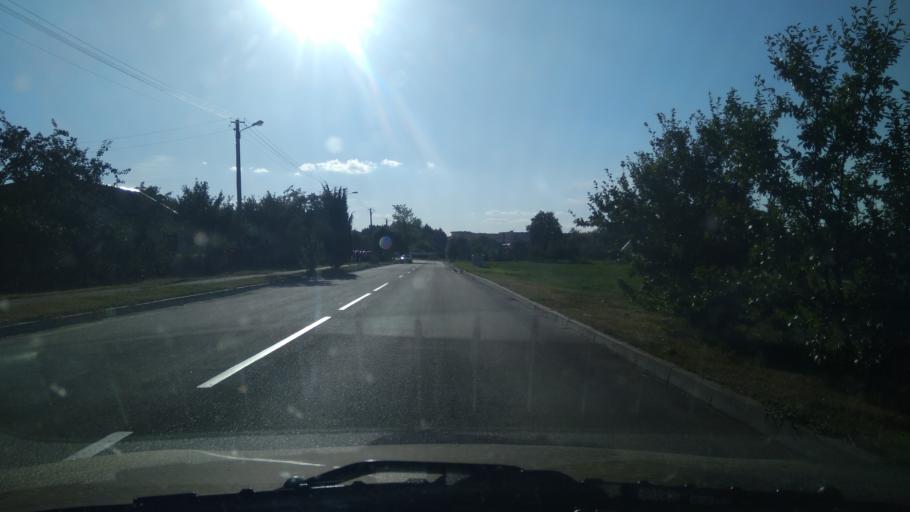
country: BY
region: Brest
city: Byaroza
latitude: 52.5370
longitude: 24.9825
